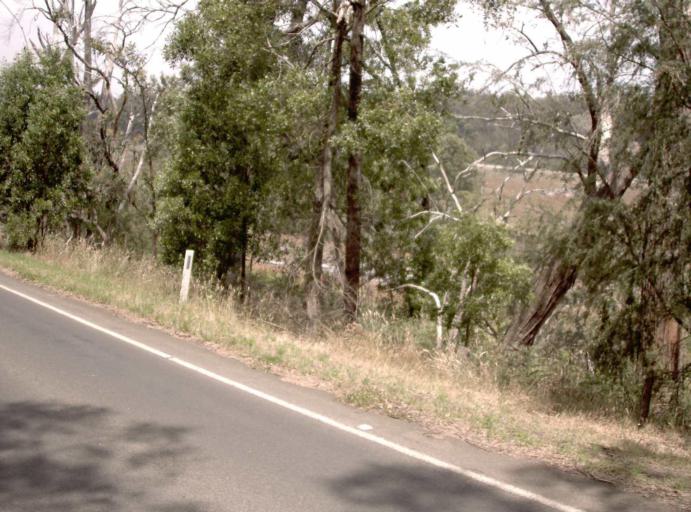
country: AU
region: Victoria
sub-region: Latrobe
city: Traralgon
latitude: -38.2836
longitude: 146.6951
